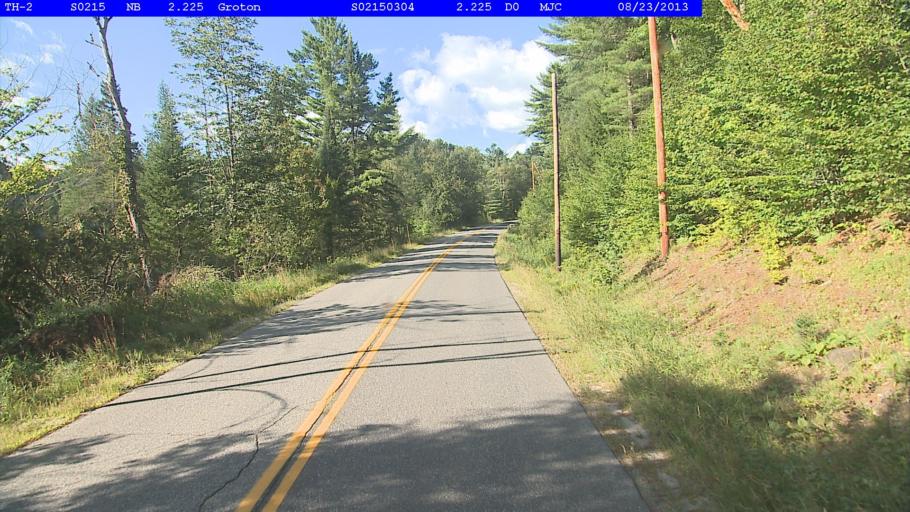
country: US
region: New Hampshire
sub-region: Grafton County
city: Woodsville
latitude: 44.2395
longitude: -72.1829
